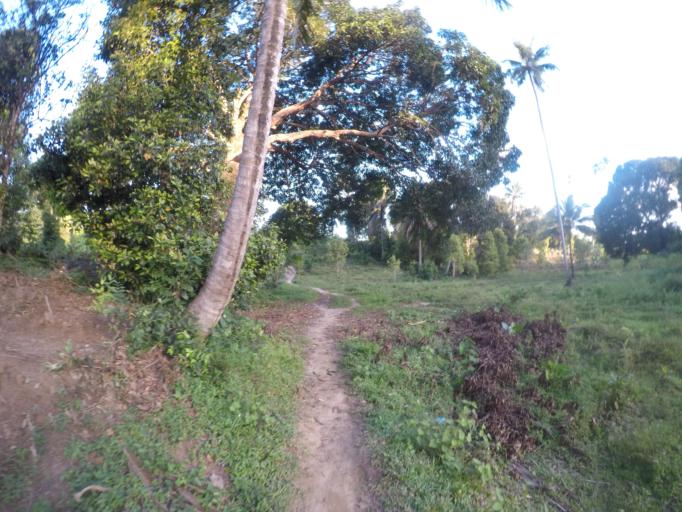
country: TZ
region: Pemba South
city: Mtambile
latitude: -5.3785
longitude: 39.7057
